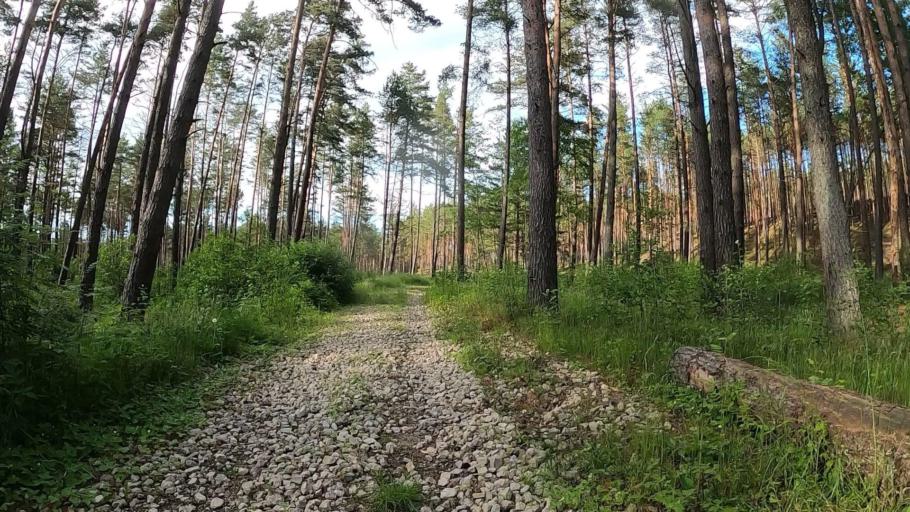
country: LV
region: Riga
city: Jaunciems
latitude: 57.0564
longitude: 24.1245
